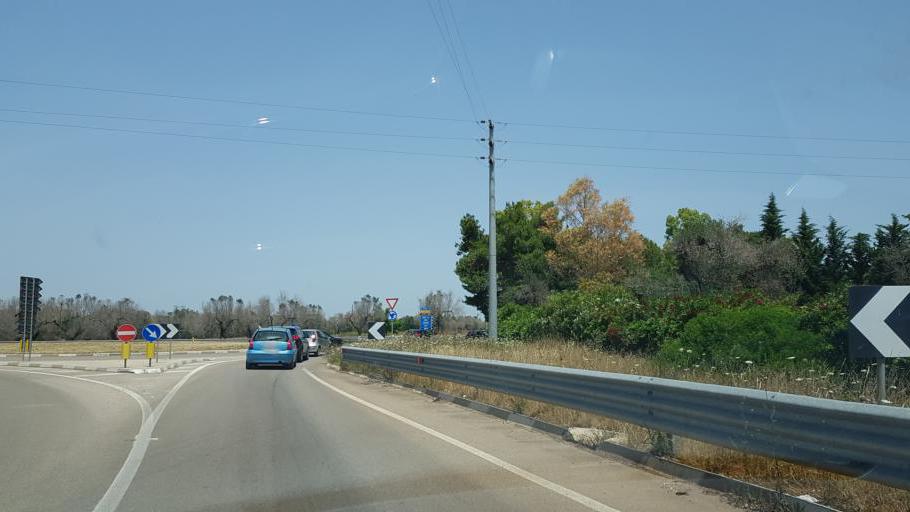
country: IT
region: Apulia
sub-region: Provincia di Lecce
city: Veglie
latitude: 40.3259
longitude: 17.9254
